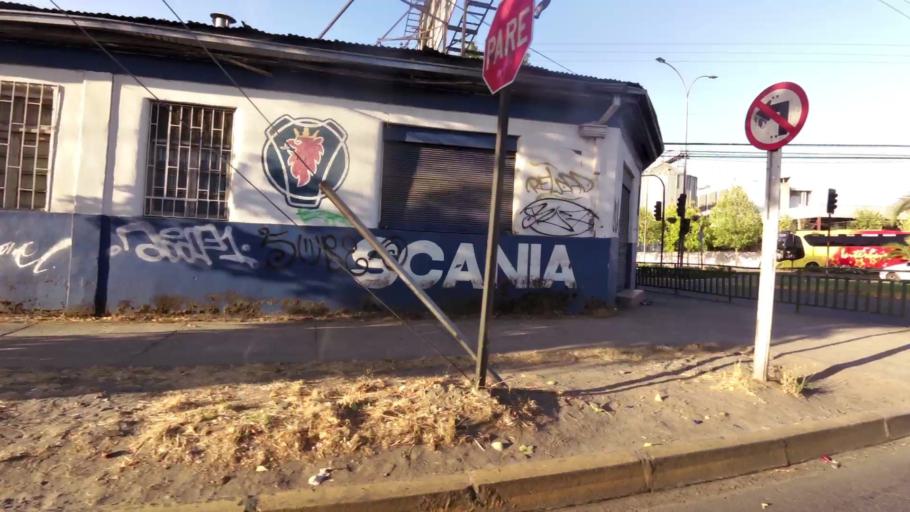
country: CL
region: Maule
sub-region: Provincia de Talca
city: Talca
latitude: -35.4312
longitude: -71.6402
